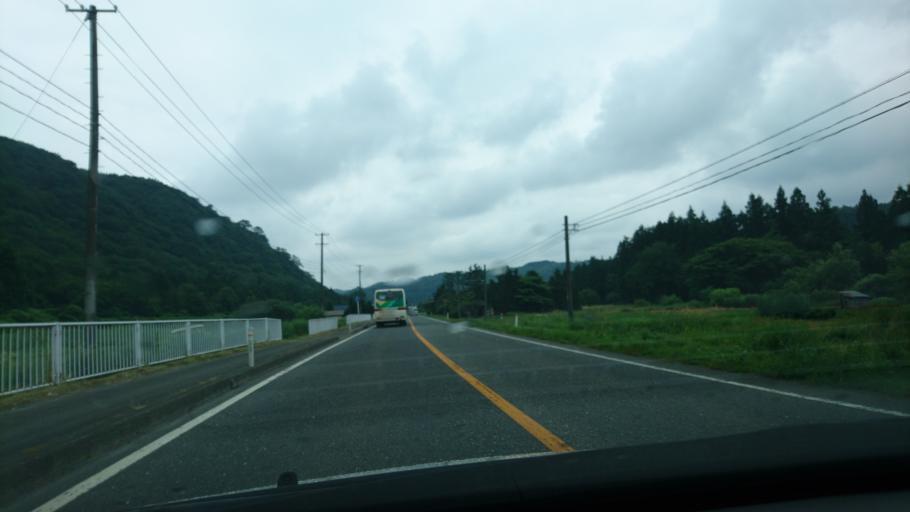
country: JP
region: Miyagi
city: Furukawa
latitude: 38.7228
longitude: 140.8004
